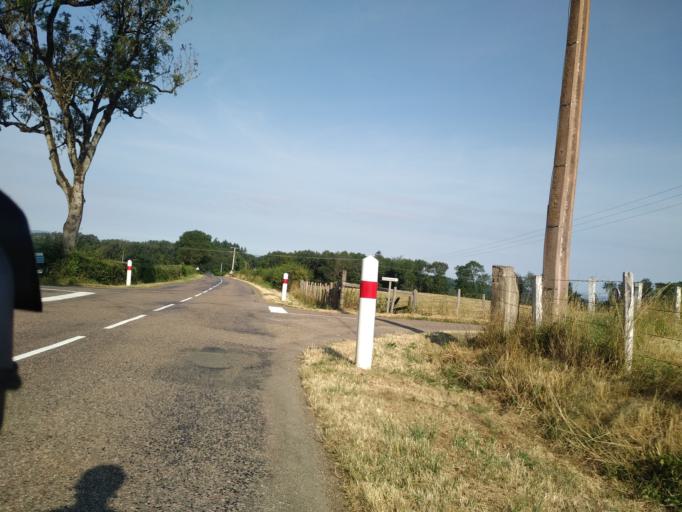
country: FR
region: Rhone-Alpes
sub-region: Departement de la Loire
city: Saint-Nizier-sous-Charlieu
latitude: 46.2394
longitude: 4.1336
